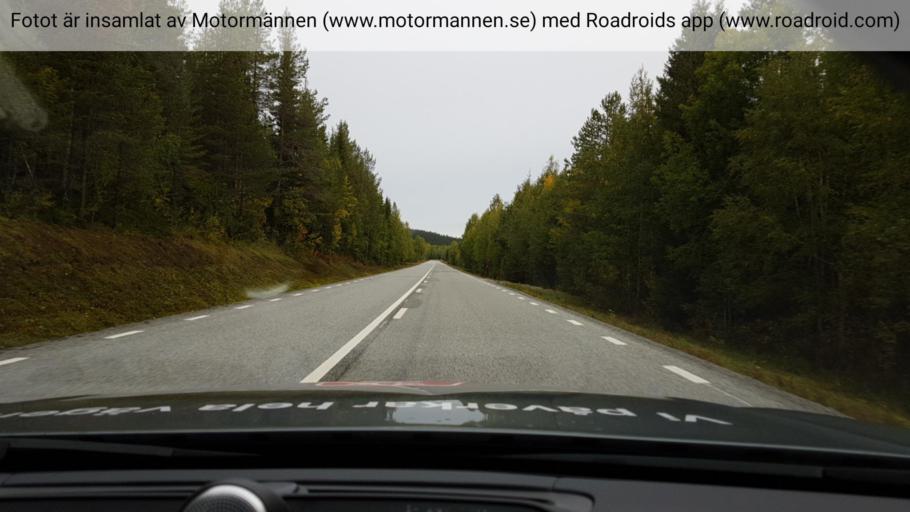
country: SE
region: Jaemtland
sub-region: Stroemsunds Kommun
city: Stroemsund
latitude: 64.1487
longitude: 15.6825
